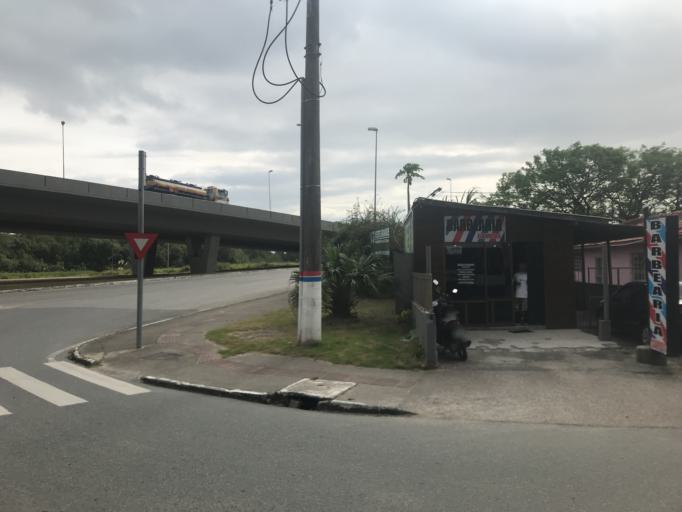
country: BR
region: Santa Catarina
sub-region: Florianopolis
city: Costeira do Pirajubae
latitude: -27.6464
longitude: -48.5217
